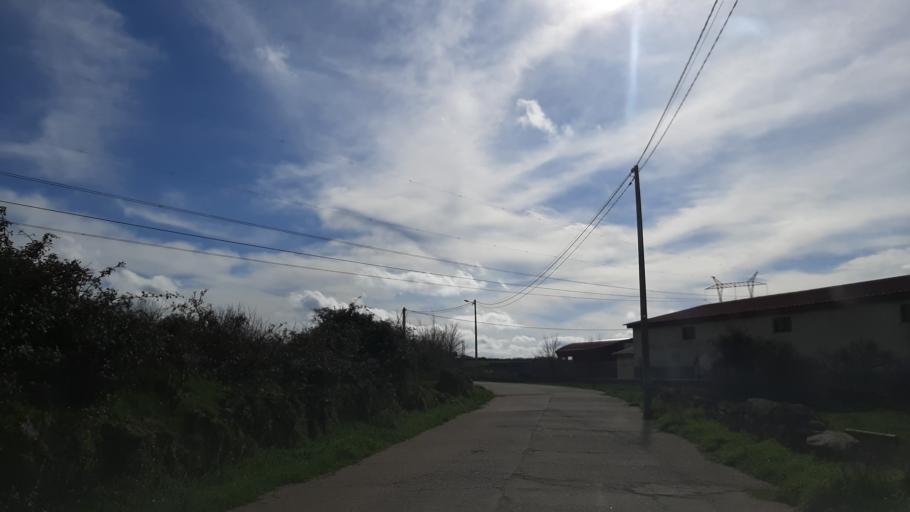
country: ES
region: Castille and Leon
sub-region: Provincia de Salamanca
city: Villarino de los Aires
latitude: 41.2455
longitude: -6.5237
